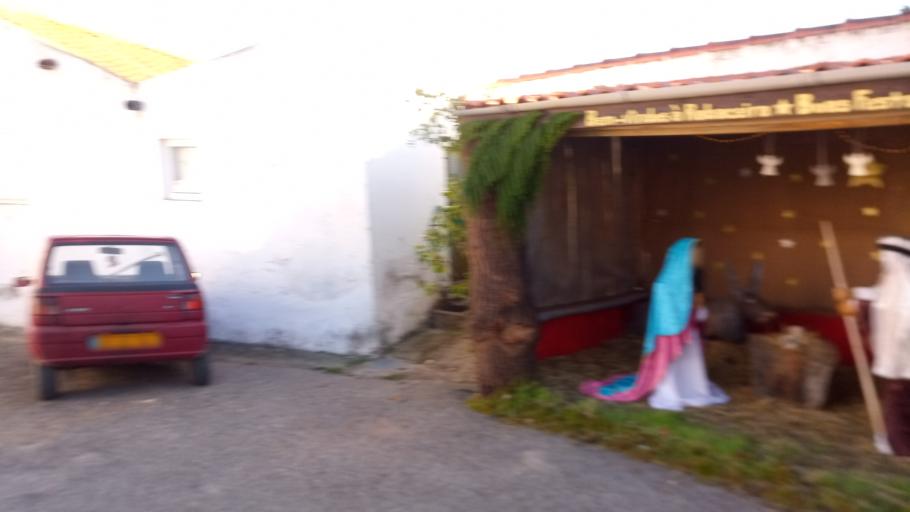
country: PT
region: Santarem
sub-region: Rio Maior
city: Rio Maior
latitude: 39.3460
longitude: -9.0171
